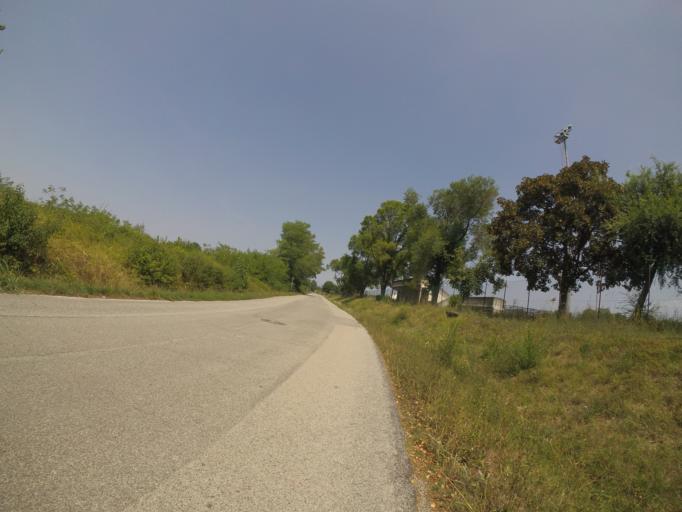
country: IT
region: Friuli Venezia Giulia
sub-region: Provincia di Udine
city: Basiliano-Vissandone
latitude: 46.0205
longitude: 13.1020
